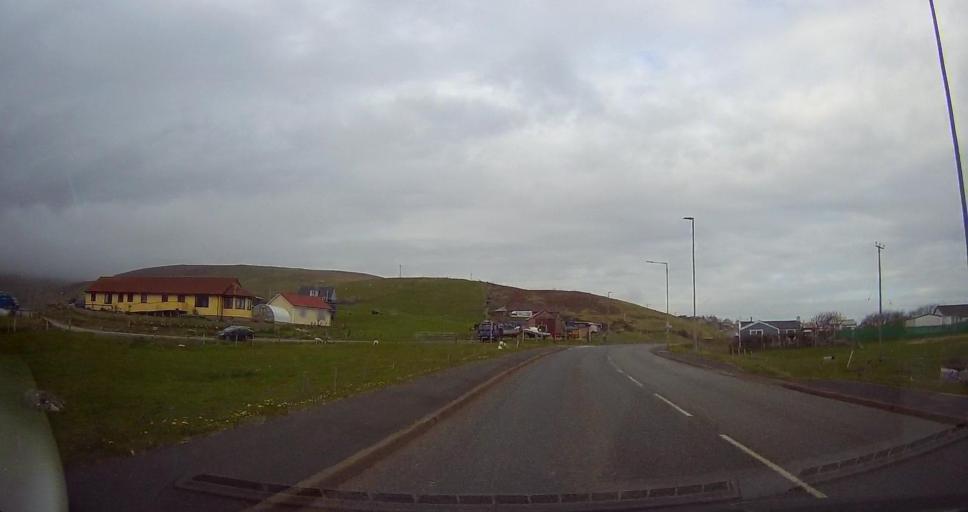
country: GB
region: Scotland
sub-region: Shetland Islands
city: Sandwick
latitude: 60.0395
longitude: -1.2297
